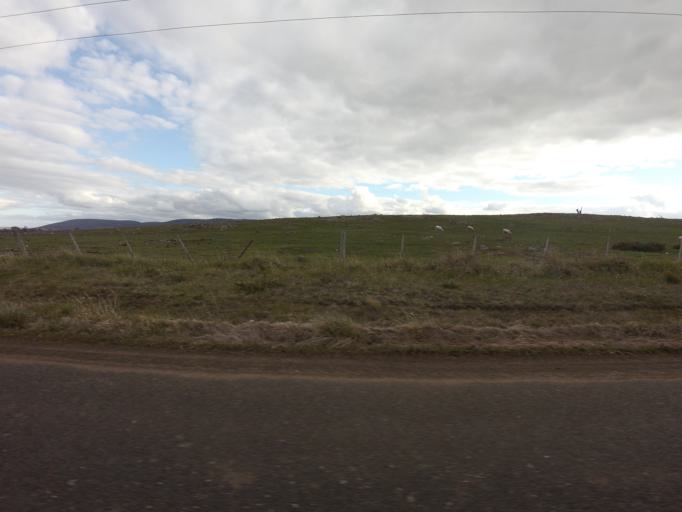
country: AU
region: Tasmania
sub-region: Northern Midlands
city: Evandale
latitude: -41.8968
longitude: 147.4347
